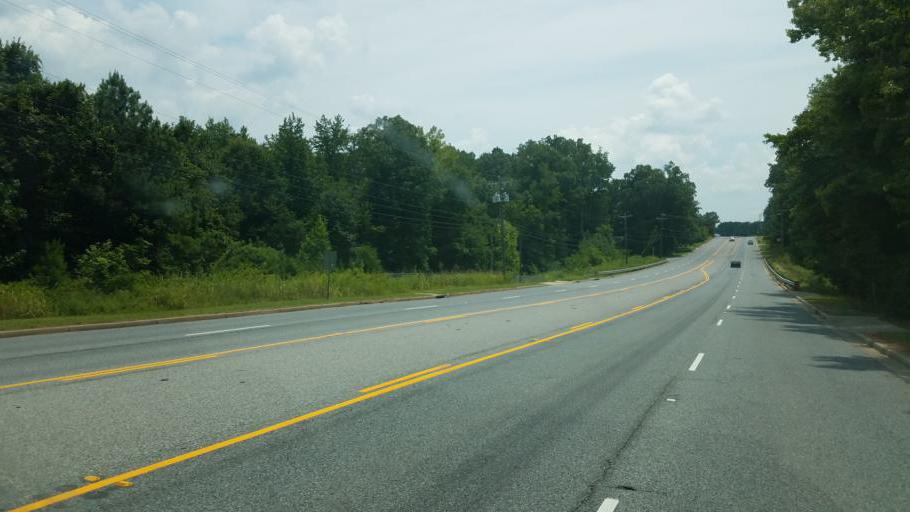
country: US
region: South Carolina
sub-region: York County
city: York
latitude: 35.0187
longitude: -81.2743
